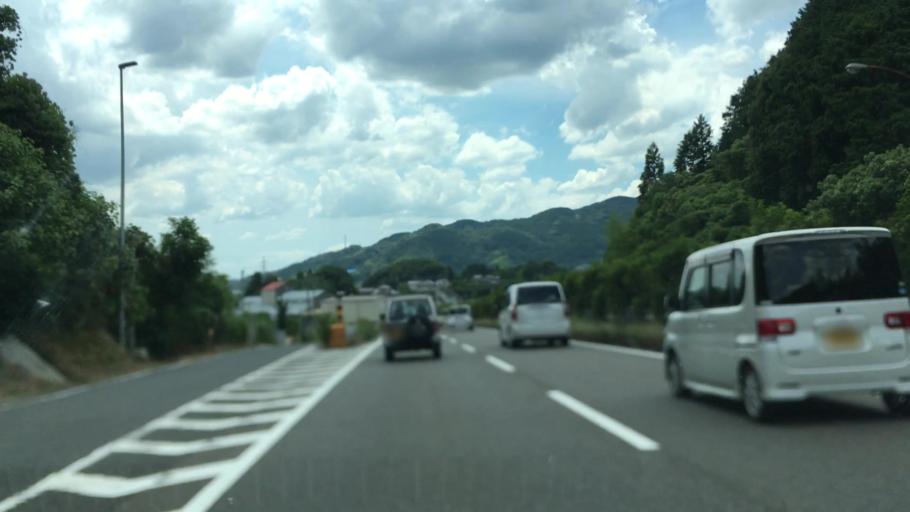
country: JP
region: Saga Prefecture
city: Tosu
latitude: 33.4283
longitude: 130.5185
